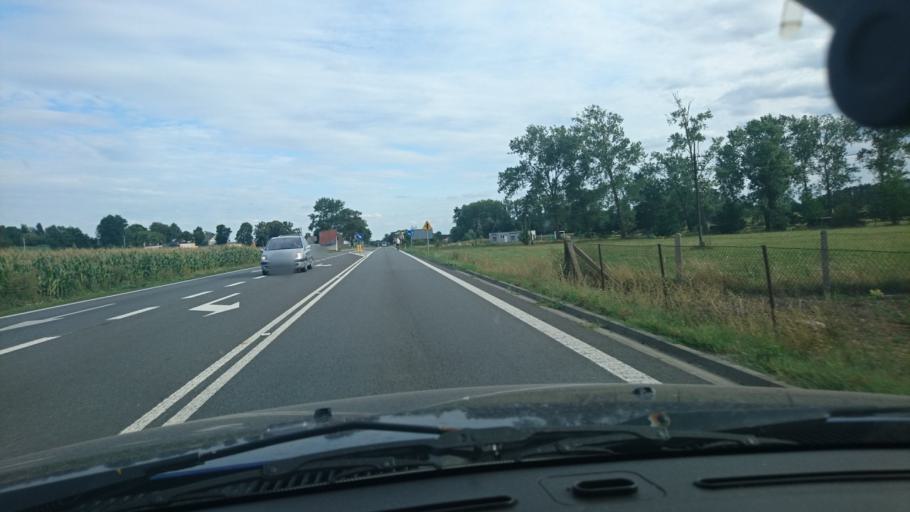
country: PL
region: Greater Poland Voivodeship
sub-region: Powiat ostrzeszowski
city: Ostrzeszow
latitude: 51.3890
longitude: 17.9467
